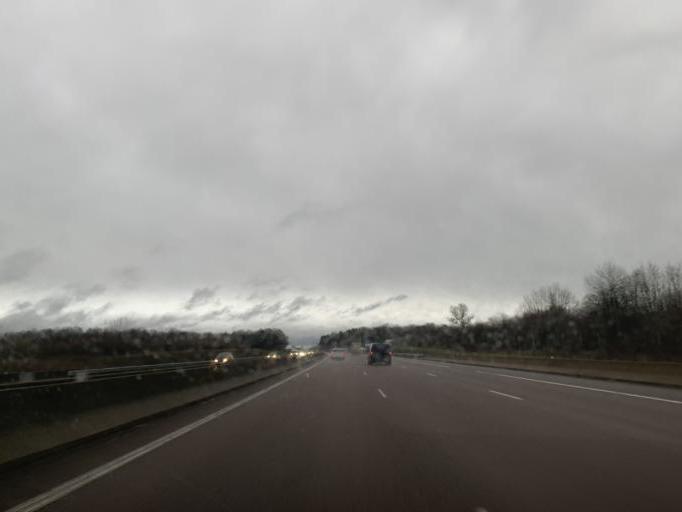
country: FR
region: Champagne-Ardenne
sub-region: Departement de la Haute-Marne
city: Langres
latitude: 47.7983
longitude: 5.2247
